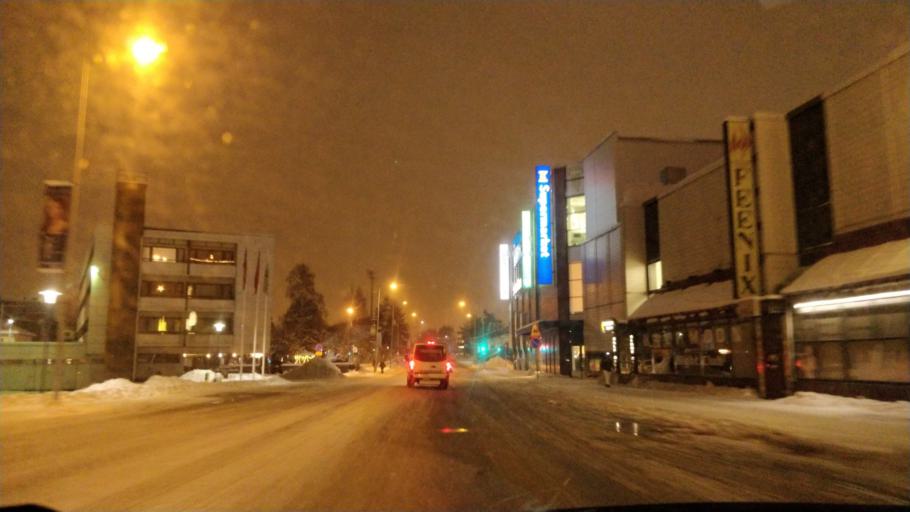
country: FI
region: Lapland
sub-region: Rovaniemi
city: Rovaniemi
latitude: 66.5028
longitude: 25.7261
